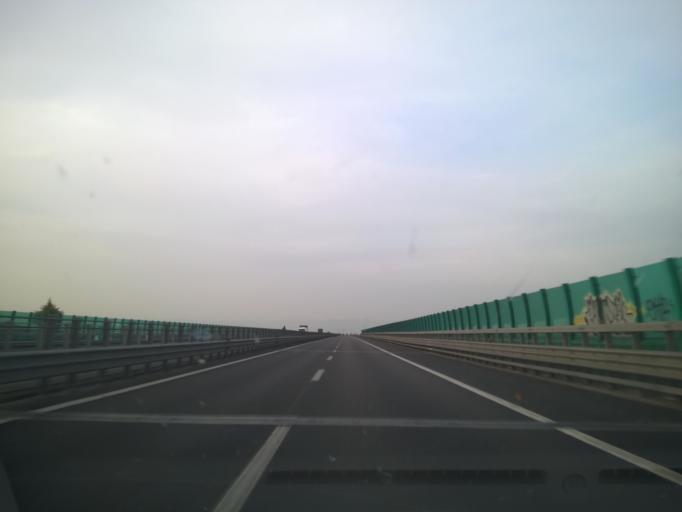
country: IT
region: Veneto
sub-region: Provincia di Vicenza
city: Torri di Quartesolo
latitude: 45.5176
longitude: 11.6231
